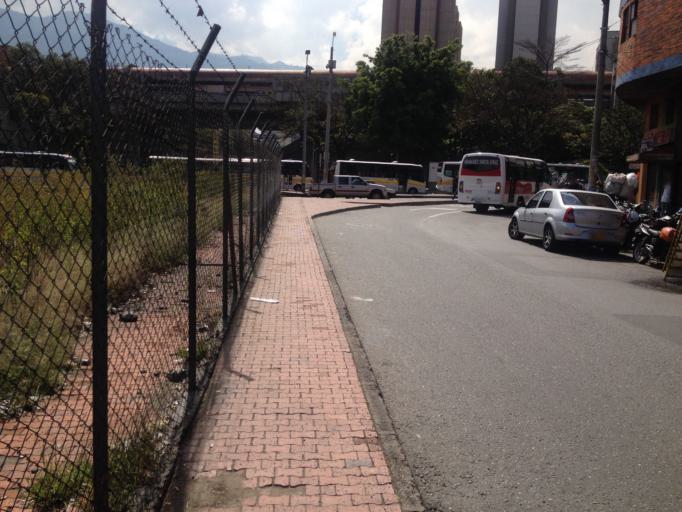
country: CO
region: Antioquia
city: Medellin
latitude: 6.2570
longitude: -75.5672
